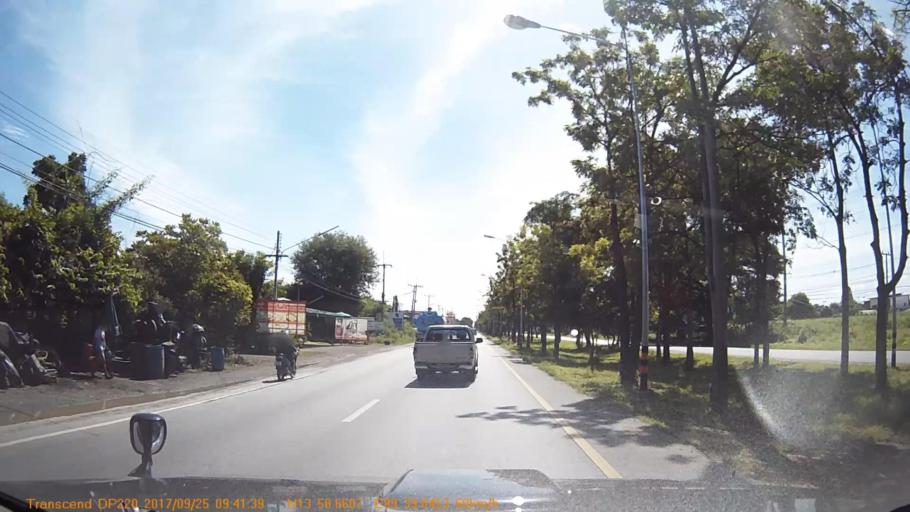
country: TH
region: Kanchanaburi
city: Tha Muang
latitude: 13.9776
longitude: 99.6512
